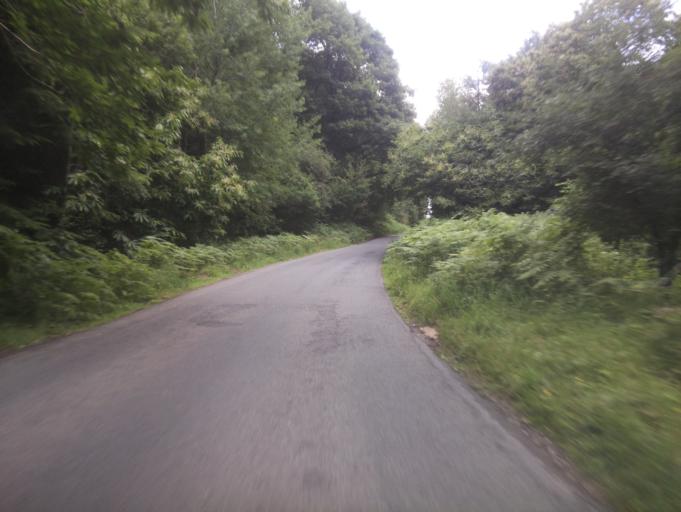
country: GB
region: England
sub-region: Gloucestershire
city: Cinderford
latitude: 51.8048
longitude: -2.4912
